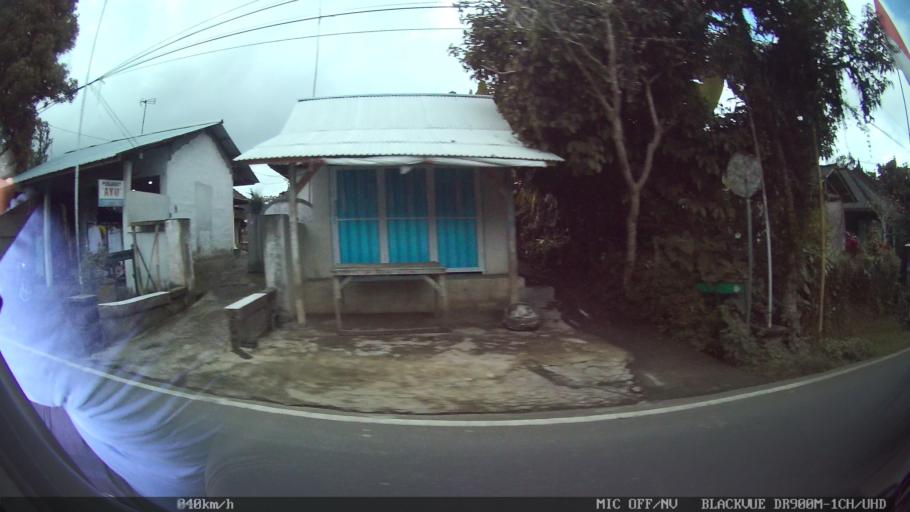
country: ID
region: Bali
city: Petang
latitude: -8.3722
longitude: 115.2239
